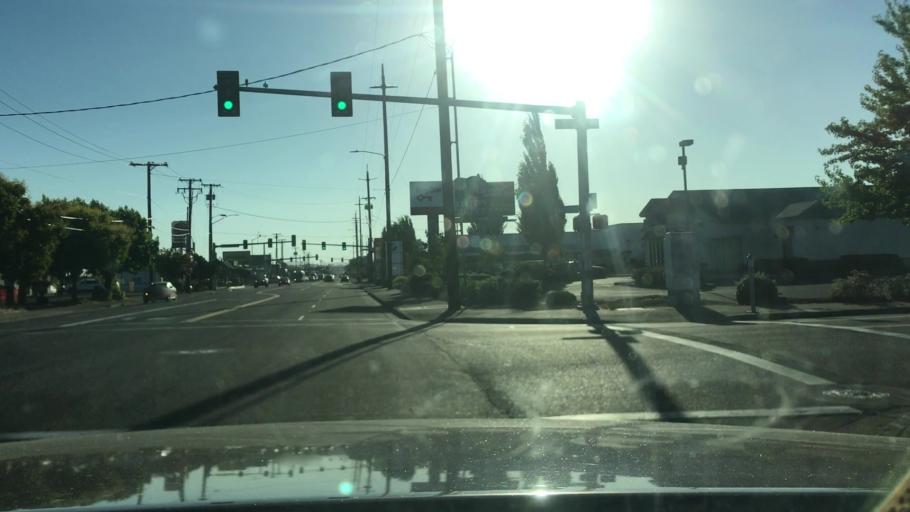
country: US
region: Oregon
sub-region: Lane County
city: Eugene
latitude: 44.0480
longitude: -123.1337
